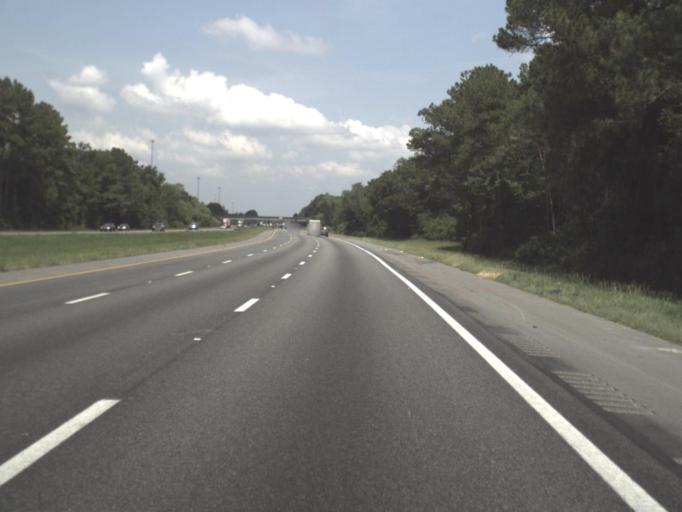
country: US
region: Georgia
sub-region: Echols County
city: Statenville
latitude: 30.6094
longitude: -83.1361
